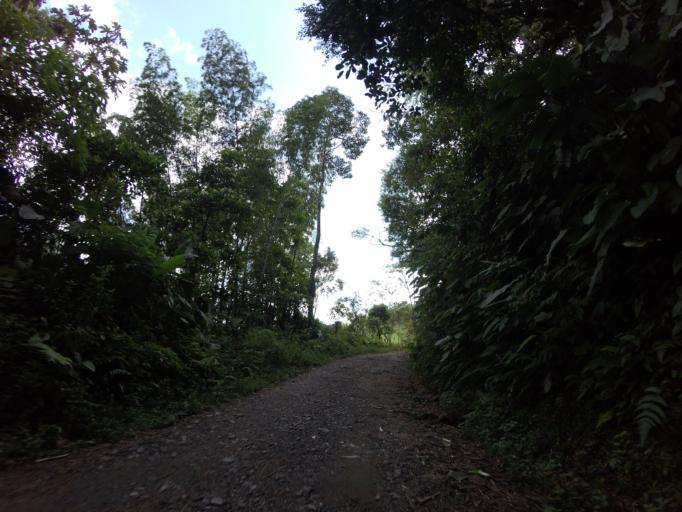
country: CO
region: Antioquia
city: Narino
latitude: 5.5137
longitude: -75.1945
